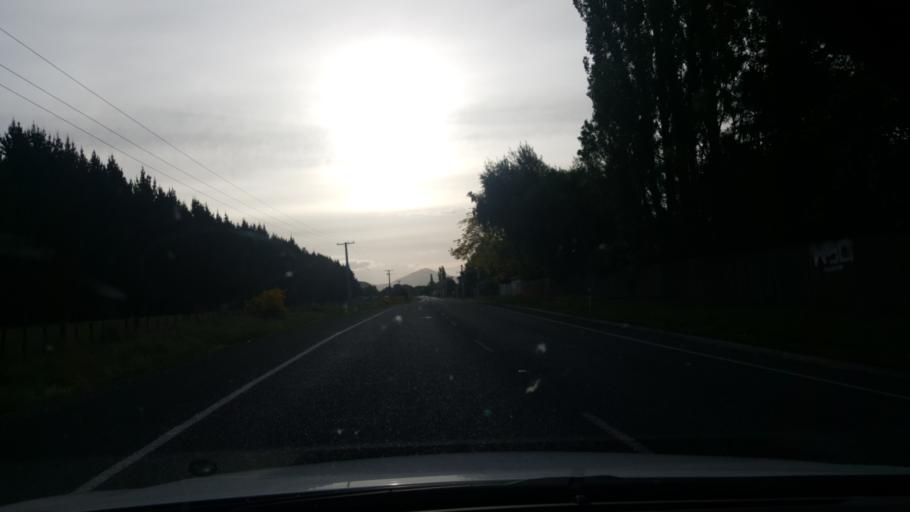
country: NZ
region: Waikato
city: Turangi
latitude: -38.9092
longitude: 175.9122
